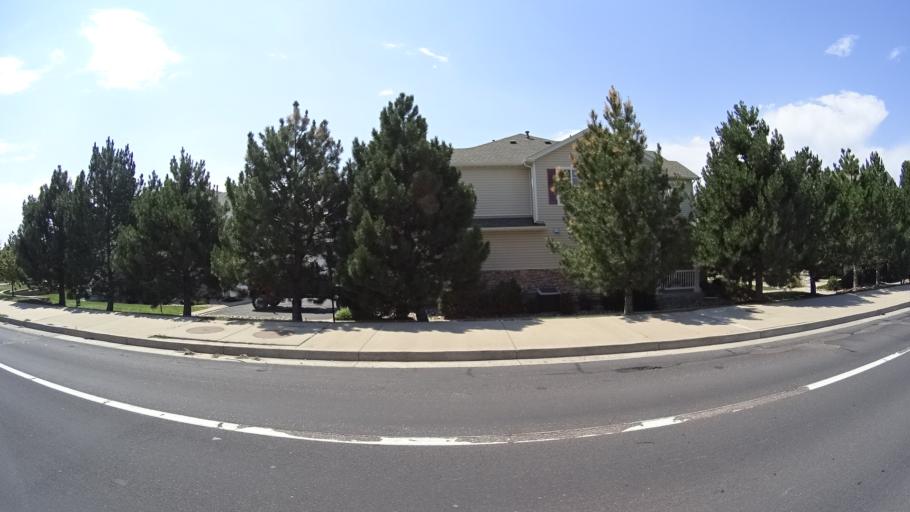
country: US
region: Colorado
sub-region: El Paso County
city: Cimarron Hills
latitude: 38.9258
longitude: -104.7113
